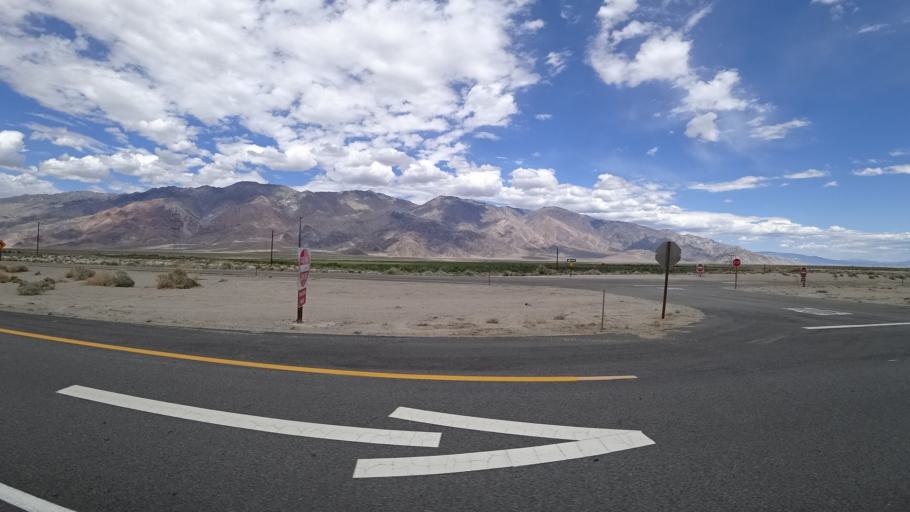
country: US
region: California
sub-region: Inyo County
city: Lone Pine
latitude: 36.6688
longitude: -118.0949
